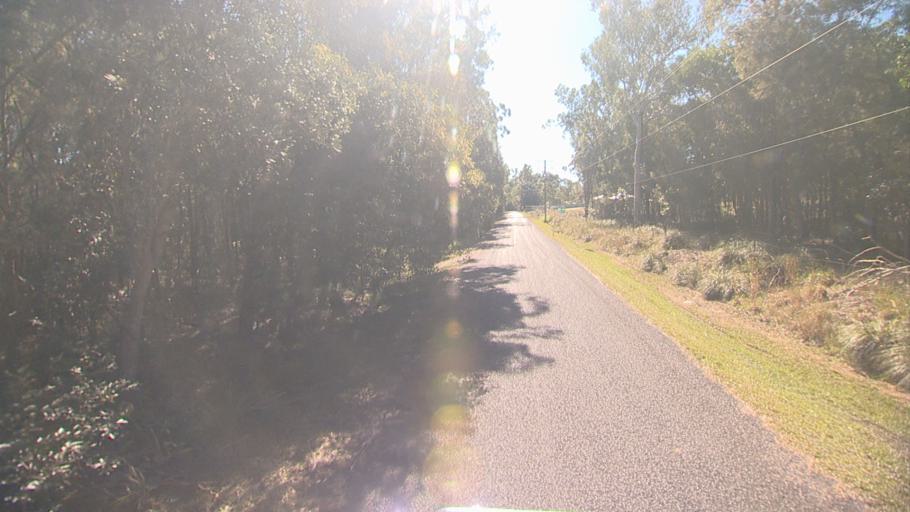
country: AU
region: Queensland
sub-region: Logan
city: Park Ridge South
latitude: -27.6899
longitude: 153.0056
